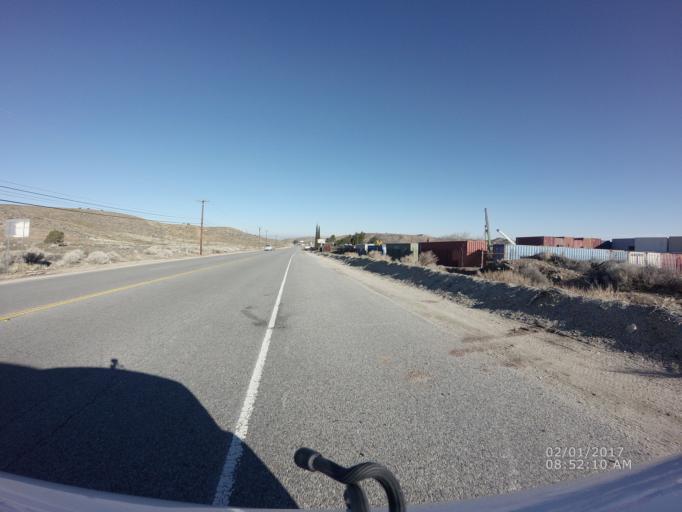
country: US
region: California
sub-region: Los Angeles County
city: Vincent
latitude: 34.5240
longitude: -118.0979
